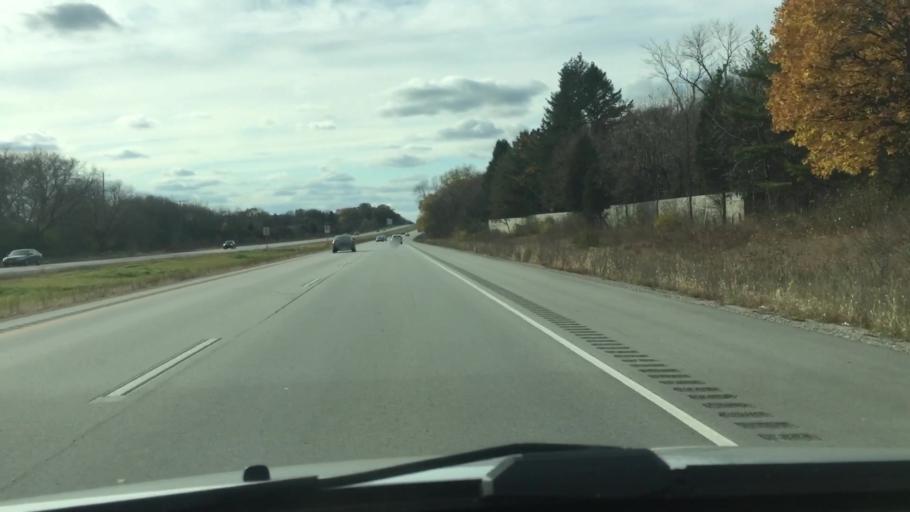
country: US
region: Wisconsin
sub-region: Waukesha County
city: Nashotah
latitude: 43.1028
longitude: -88.3827
